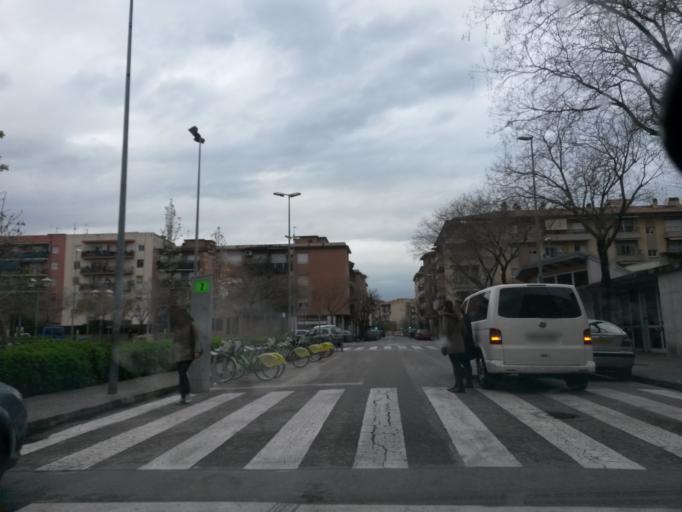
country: ES
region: Catalonia
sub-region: Provincia de Girona
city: Salt
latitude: 41.9733
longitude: 2.8072
